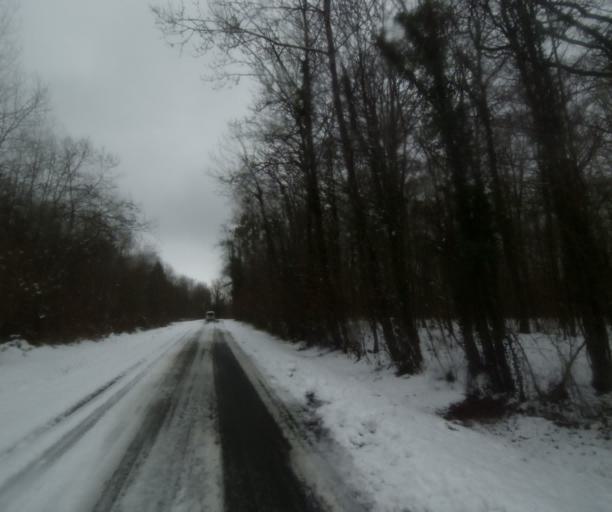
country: FR
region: Champagne-Ardenne
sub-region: Departement de la Haute-Marne
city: Laneuville-a-Remy
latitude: 48.5106
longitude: 4.8949
